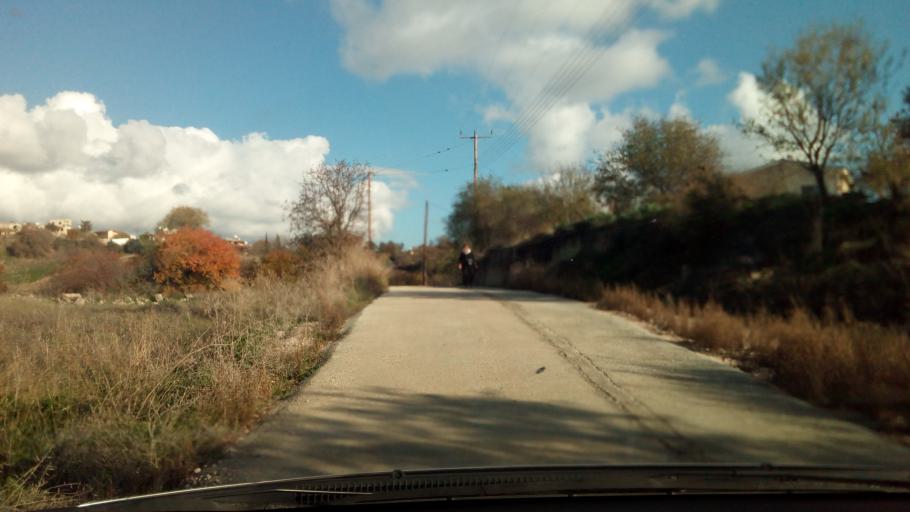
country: CY
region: Pafos
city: Polis
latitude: 34.9405
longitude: 32.4987
